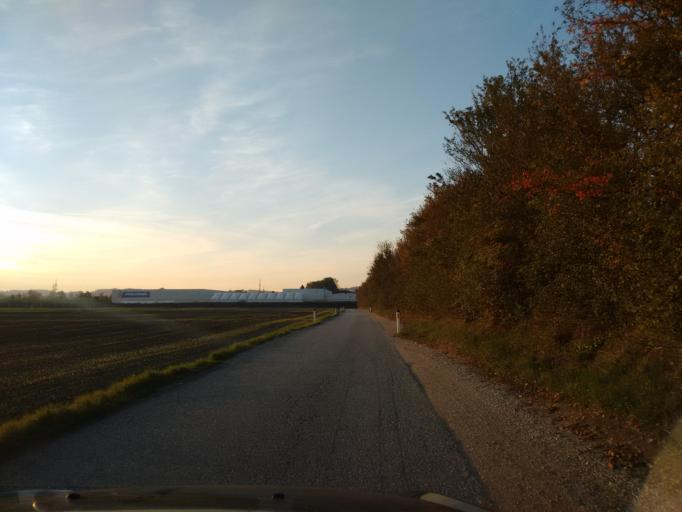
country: AT
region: Upper Austria
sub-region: Wels-Land
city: Gunskirchen
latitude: 48.1601
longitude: 13.9856
